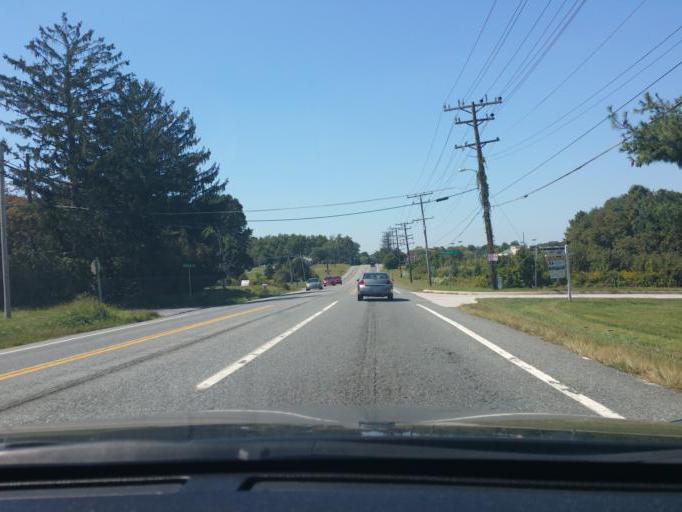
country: US
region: Maryland
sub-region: Harford County
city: Bel Air South
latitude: 39.5558
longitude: -76.2670
